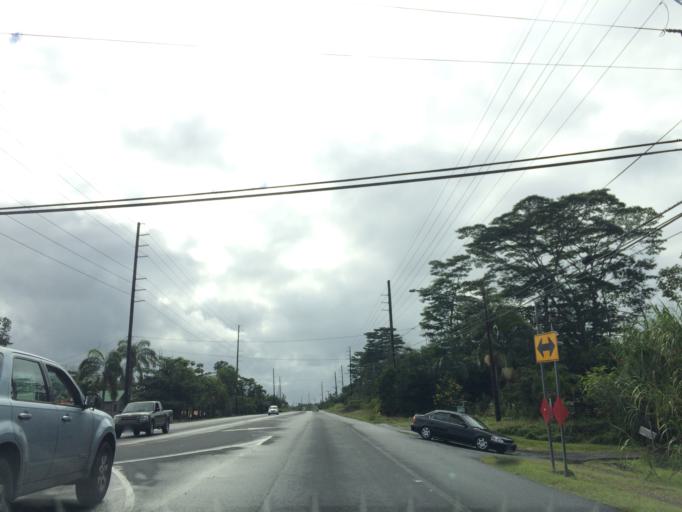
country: US
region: Hawaii
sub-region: Hawaii County
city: Orchidlands Estates
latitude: 19.5580
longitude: -154.9902
